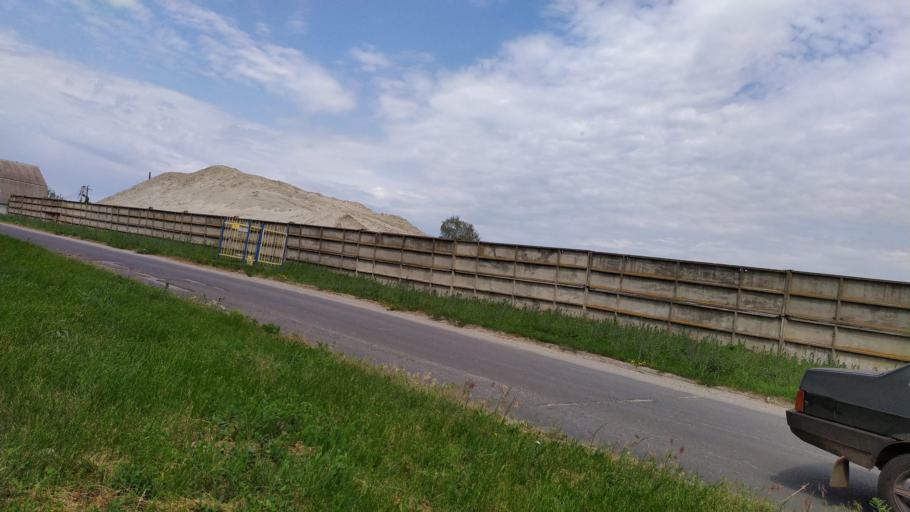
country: RU
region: Kursk
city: Kursk
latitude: 51.6587
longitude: 36.1527
